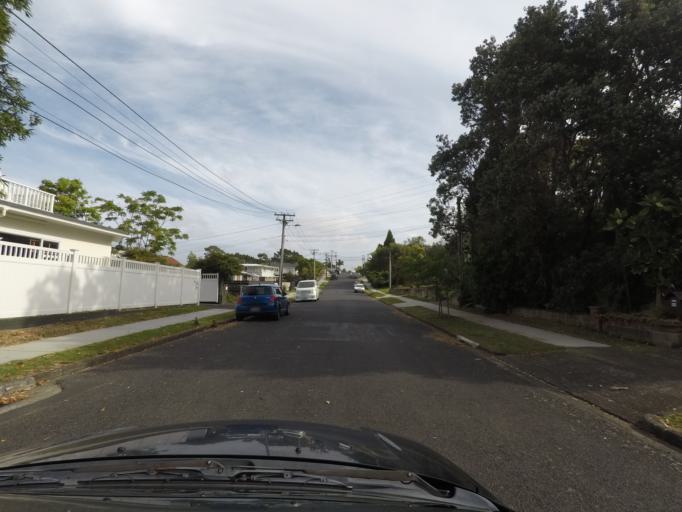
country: NZ
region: Auckland
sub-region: Auckland
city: Rosebank
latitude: -36.8970
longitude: 174.6712
